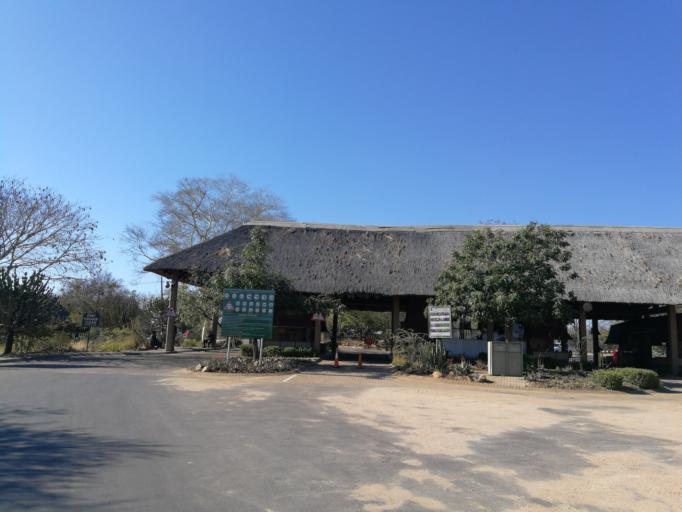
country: ZA
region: Limpopo
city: Thulamahashi
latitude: -24.9808
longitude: 31.4845
